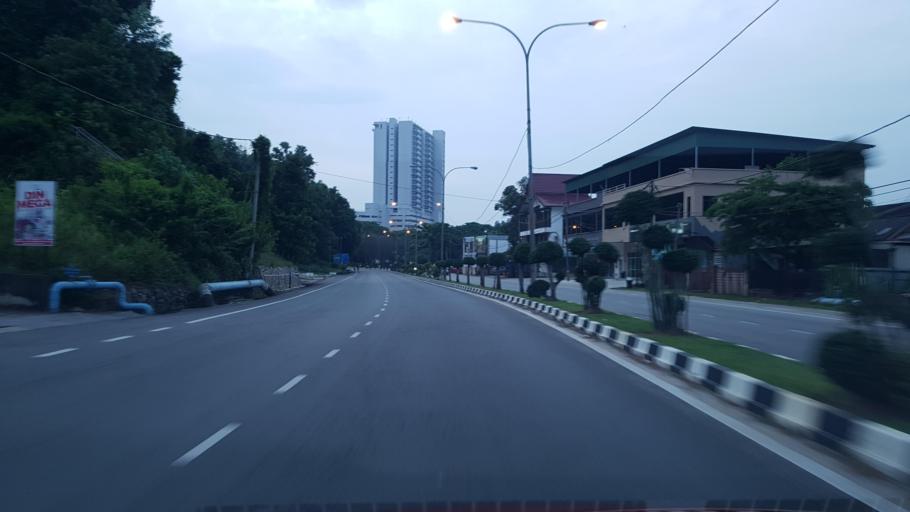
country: MY
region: Terengganu
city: Kuala Terengganu
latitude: 5.3182
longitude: 103.1440
